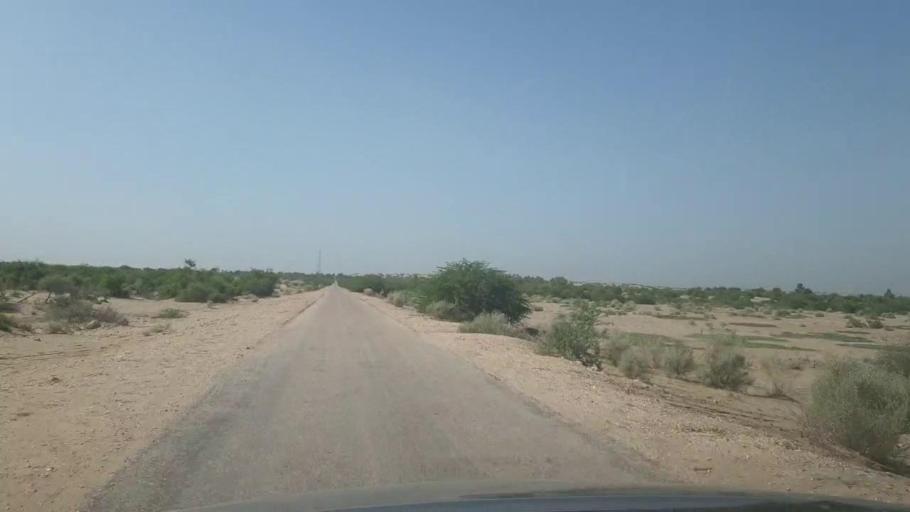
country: PK
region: Sindh
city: Rohri
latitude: 27.4196
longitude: 69.0799
